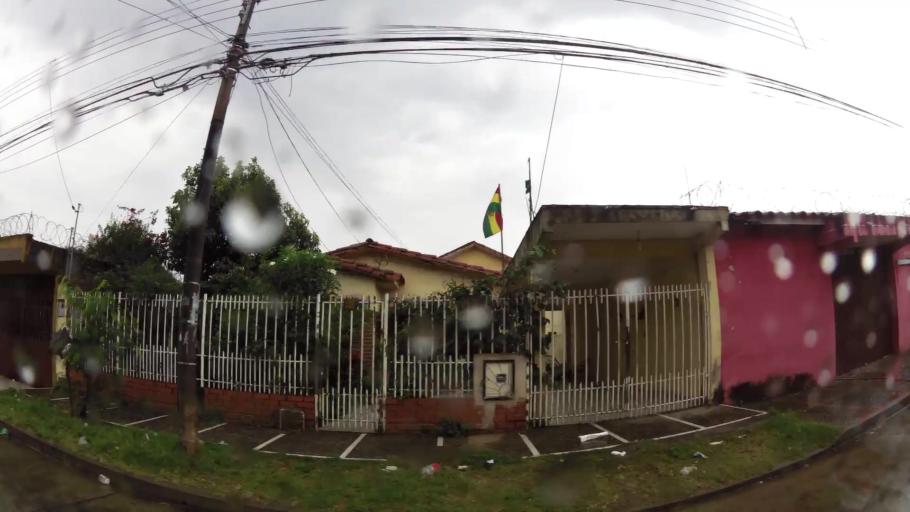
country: BO
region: Santa Cruz
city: Santa Cruz de la Sierra
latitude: -17.7937
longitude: -63.1537
